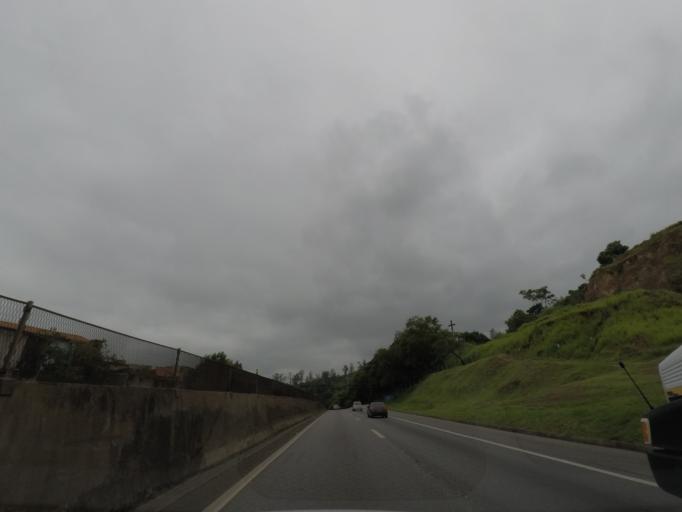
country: BR
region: Sao Paulo
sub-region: Aparecida
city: Aparecida
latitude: -22.8517
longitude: -45.2279
